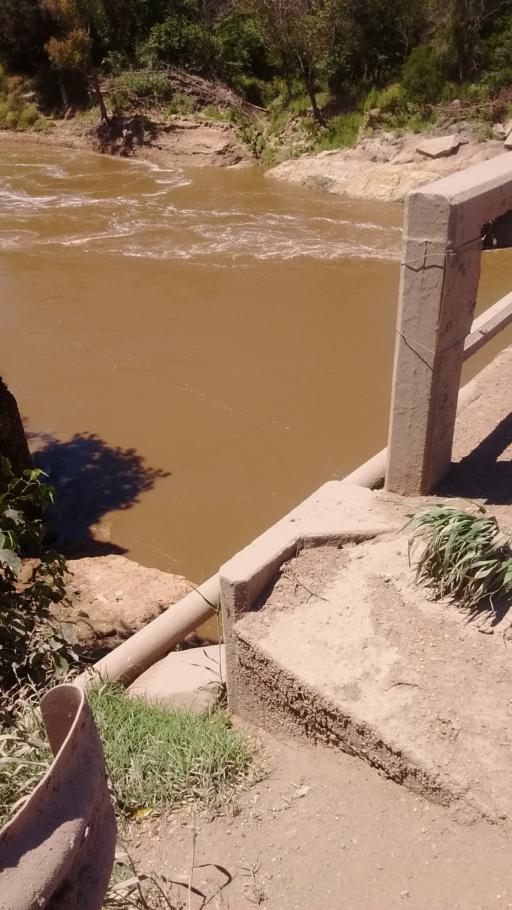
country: AR
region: Santa Fe
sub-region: Departamento de San Lorenzo
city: San Lorenzo
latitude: -32.6385
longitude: -60.8146
